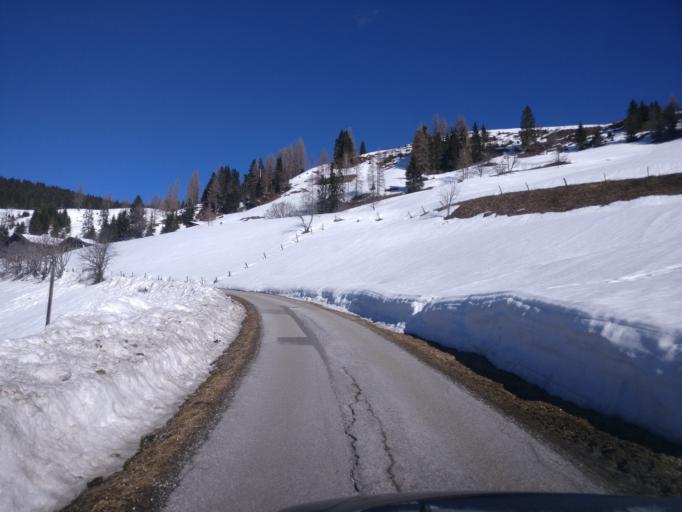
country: AT
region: Salzburg
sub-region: Politischer Bezirk Sankt Johann im Pongau
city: Wagrain
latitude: 47.3428
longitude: 13.2529
